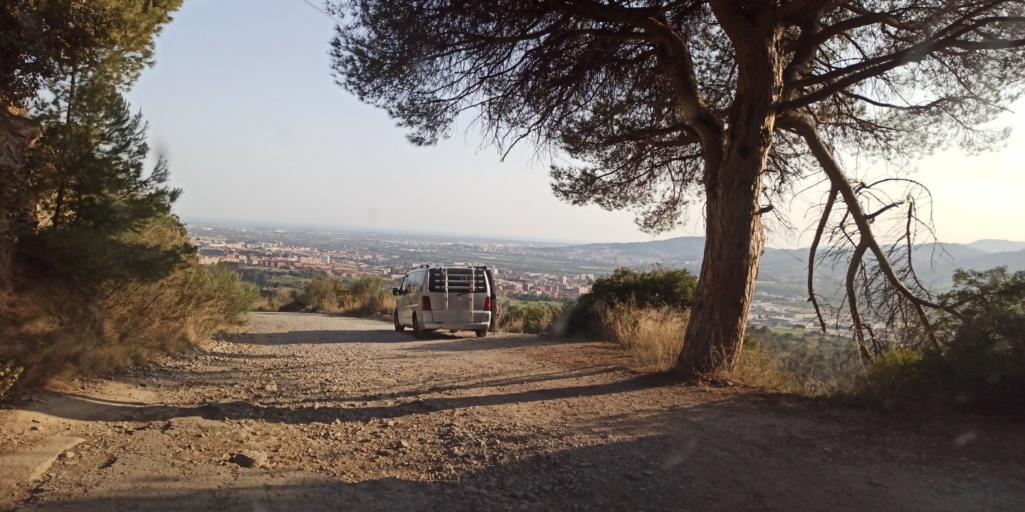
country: ES
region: Catalonia
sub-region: Provincia de Barcelona
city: Sant Feliu de Llobregat
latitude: 41.4066
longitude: 2.0518
